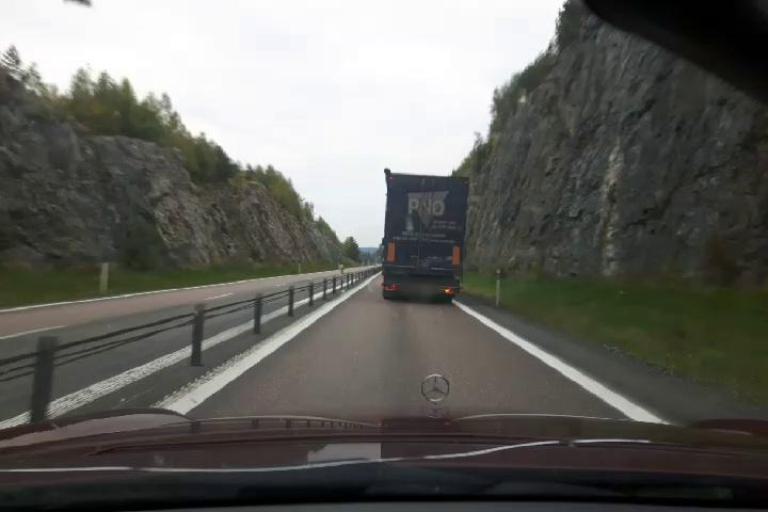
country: SE
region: Vaesternorrland
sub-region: Haernoesands Kommun
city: Haernoesand
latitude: 62.8282
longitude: 17.9683
